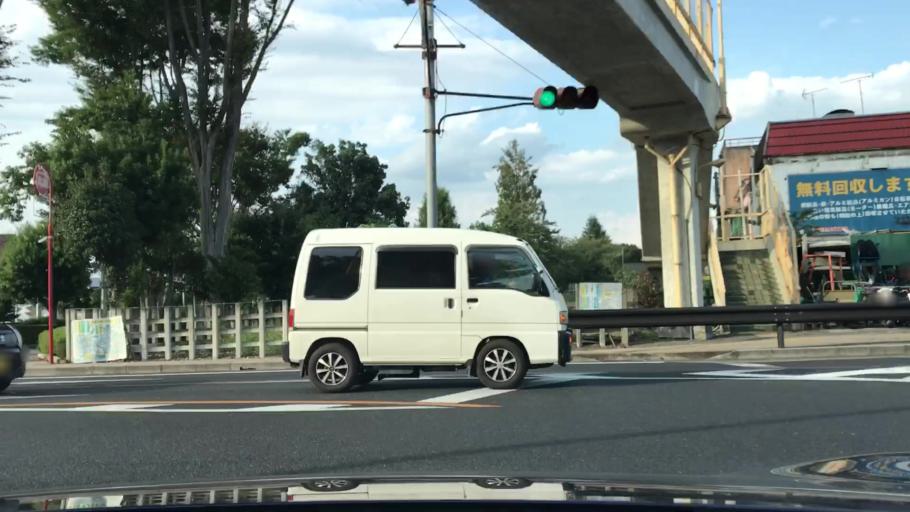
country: JP
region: Saitama
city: Menuma
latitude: 36.2573
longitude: 139.4078
